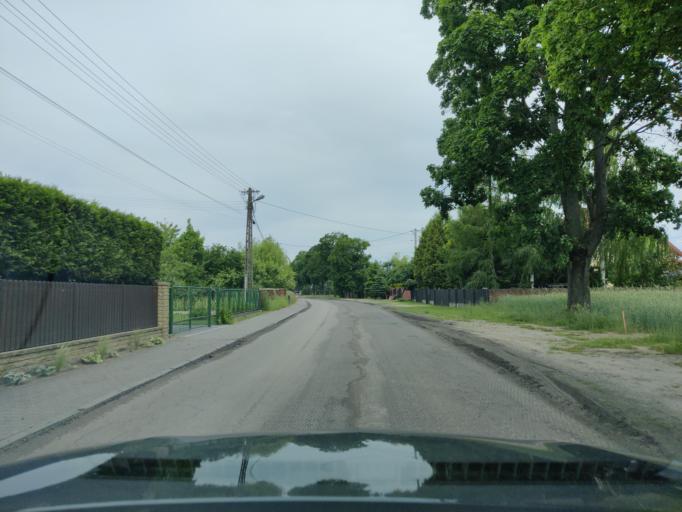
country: PL
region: Masovian Voivodeship
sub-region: Powiat wyszkowski
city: Rzasnik
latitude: 52.6894
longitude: 21.4212
